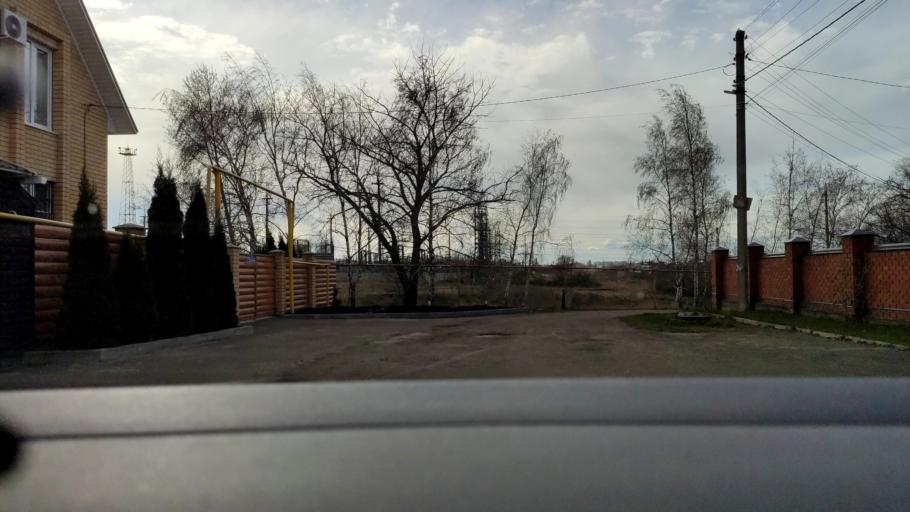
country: RU
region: Voronezj
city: Maslovka
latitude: 51.6266
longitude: 39.2808
